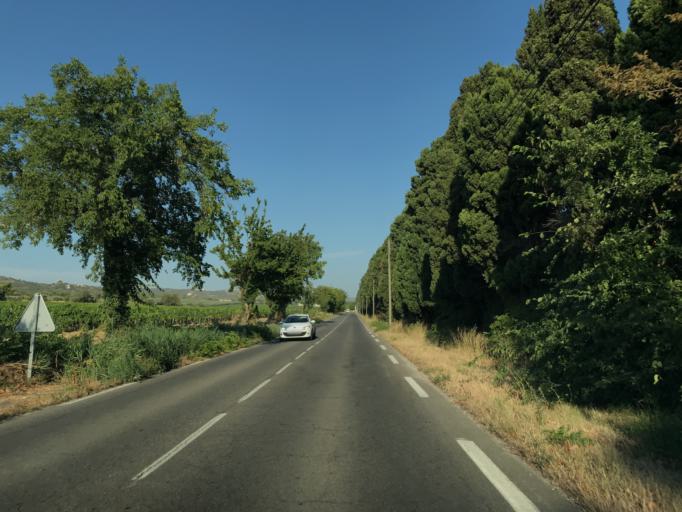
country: FR
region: Provence-Alpes-Cote d'Azur
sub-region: Departement des Bouches-du-Rhone
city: Lancon-Provence
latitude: 43.5455
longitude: 5.1392
